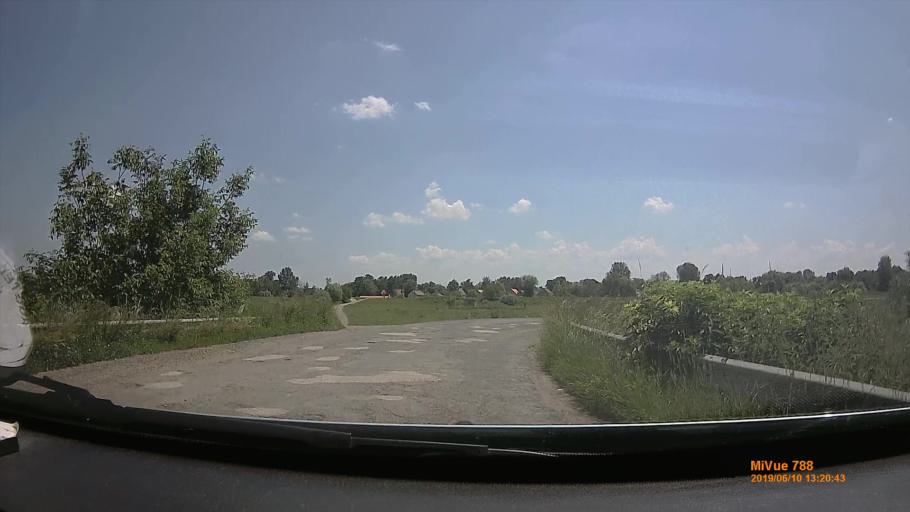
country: HU
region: Borsod-Abauj-Zemplen
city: Tiszaluc
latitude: 48.0395
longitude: 21.0800
